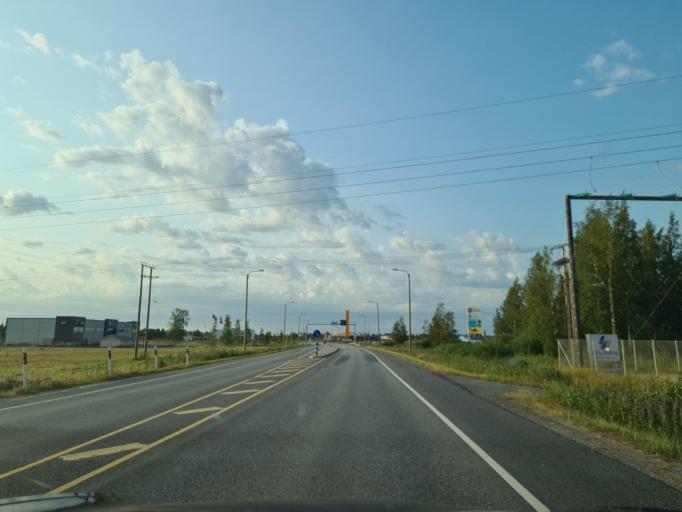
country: FI
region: Southern Ostrobothnia
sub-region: Seinaejoki
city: Kauhava
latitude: 63.0856
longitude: 23.0592
